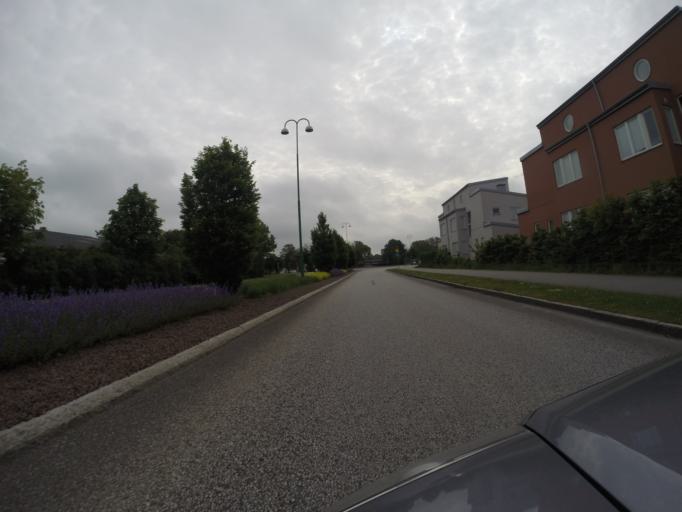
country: SE
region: Skane
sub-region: Burlovs Kommun
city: Arloev
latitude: 55.6394
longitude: 13.0624
